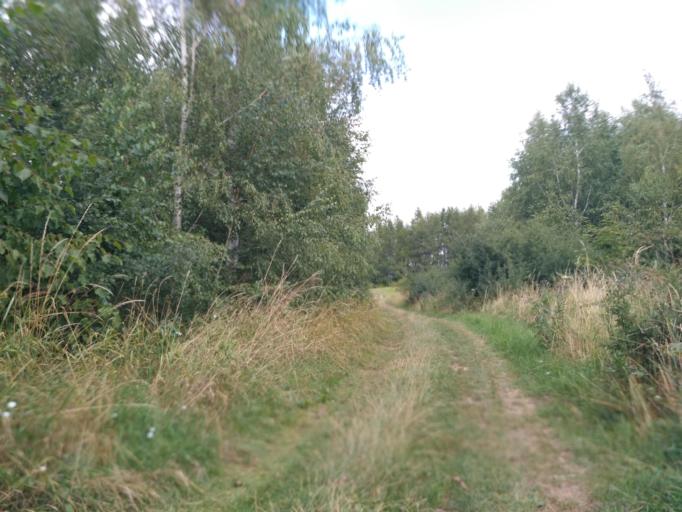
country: PL
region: Subcarpathian Voivodeship
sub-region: Powiat krosnienski
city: Iwonicz-Zdroj
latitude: 49.5771
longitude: 21.8071
